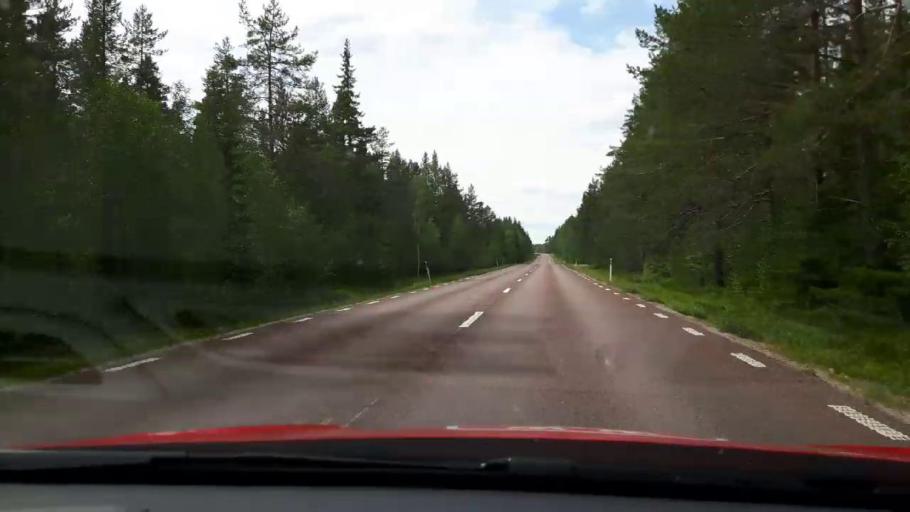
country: SE
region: Jaemtland
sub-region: Harjedalens Kommun
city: Sveg
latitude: 62.0486
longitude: 14.4943
